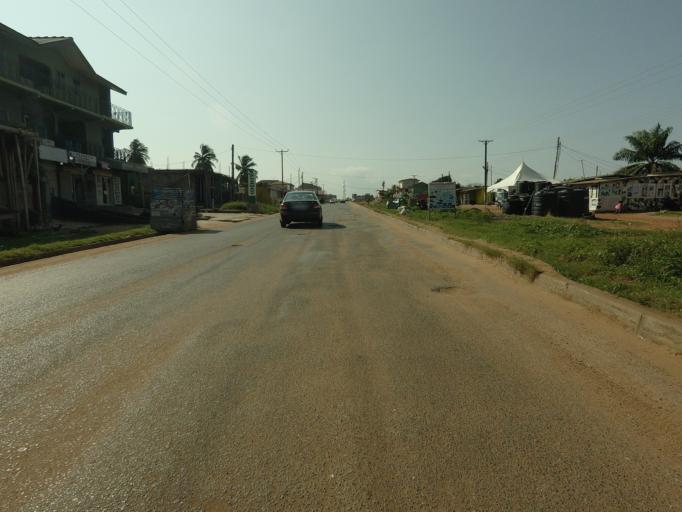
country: GH
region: Greater Accra
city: Teshi Old Town
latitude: 5.6053
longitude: -0.1055
